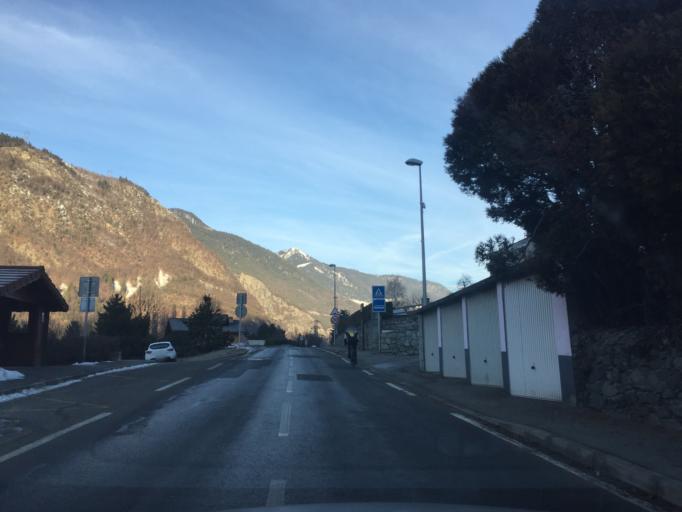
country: FR
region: Rhone-Alpes
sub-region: Departement de la Savoie
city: Aigueblanche
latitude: 45.5142
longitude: 6.4934
